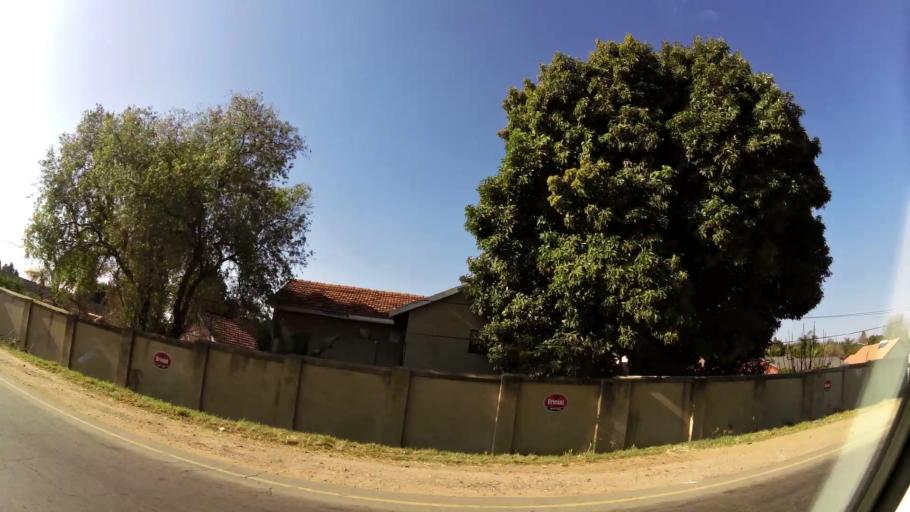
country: ZA
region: Gauteng
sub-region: City of Tshwane Metropolitan Municipality
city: Centurion
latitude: -25.8277
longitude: 28.2628
